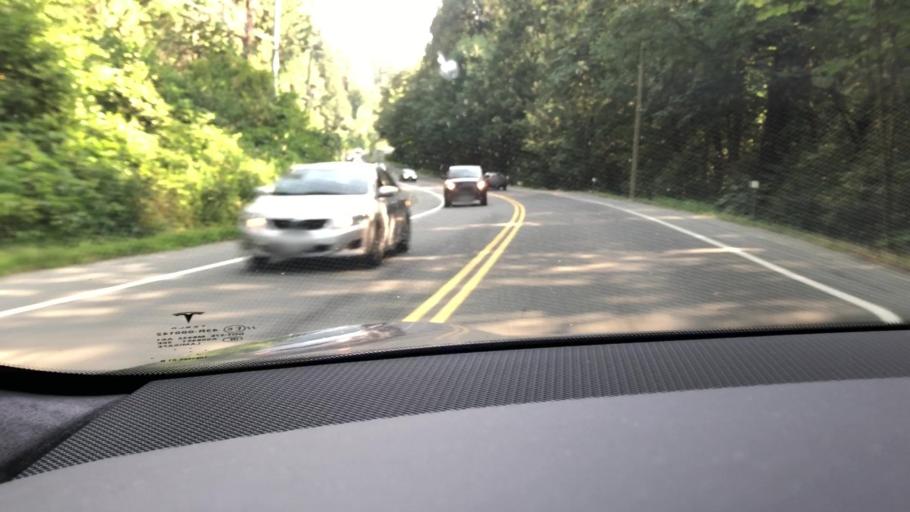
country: CA
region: British Columbia
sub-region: Fraser Valley Regional District
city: Chilliwack
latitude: 49.0820
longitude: -121.9766
